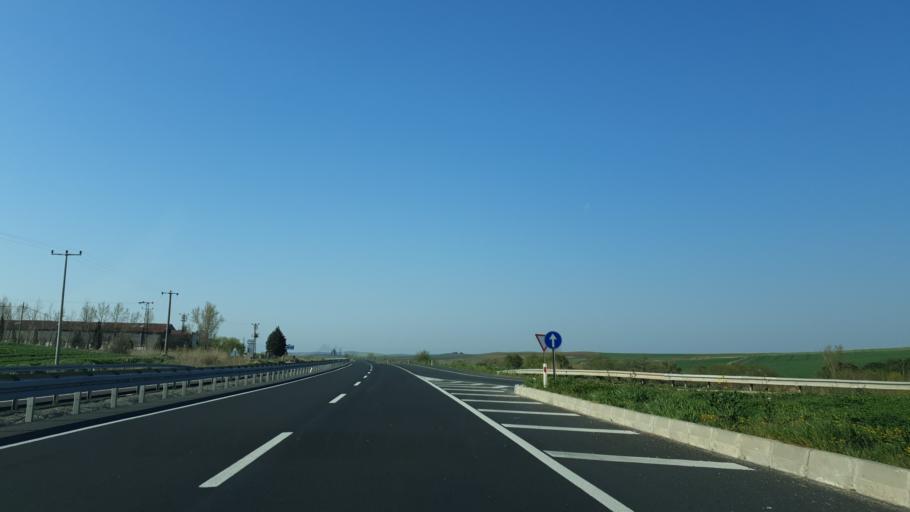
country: TR
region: Tekirdag
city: Corlu
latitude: 41.1216
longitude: 27.7518
